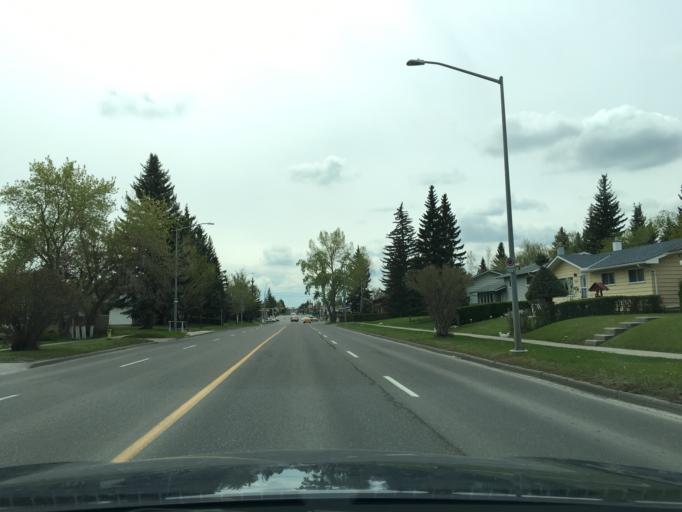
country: CA
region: Alberta
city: Calgary
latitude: 50.9664
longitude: -114.0848
